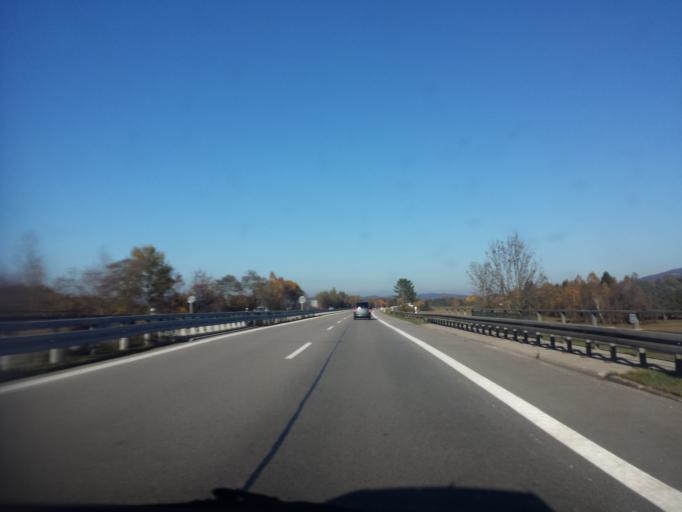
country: DE
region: Bavaria
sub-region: Upper Bavaria
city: Eschenlohe
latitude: 47.6130
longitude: 11.1834
